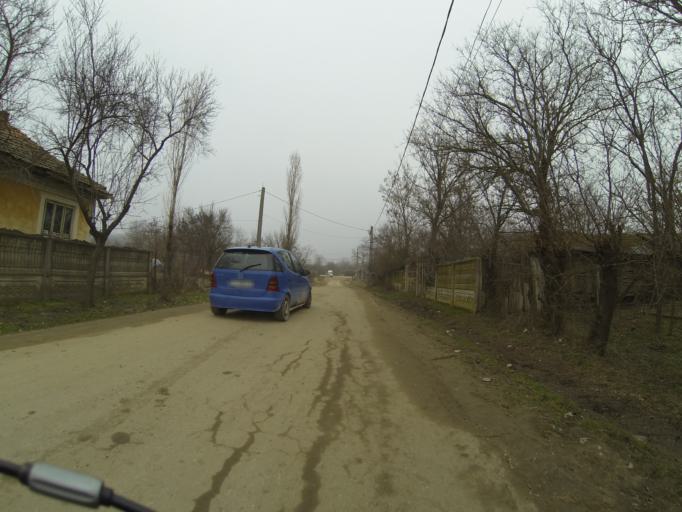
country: RO
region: Mehedinti
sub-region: Comuna Balacita
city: Gvardinita
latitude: 44.3988
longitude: 23.1448
